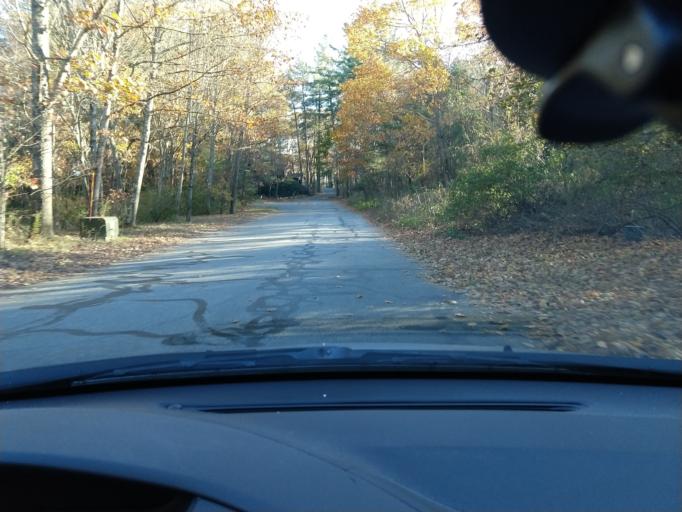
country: US
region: Massachusetts
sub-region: Middlesex County
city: Carlisle
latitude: 42.4998
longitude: -71.3223
